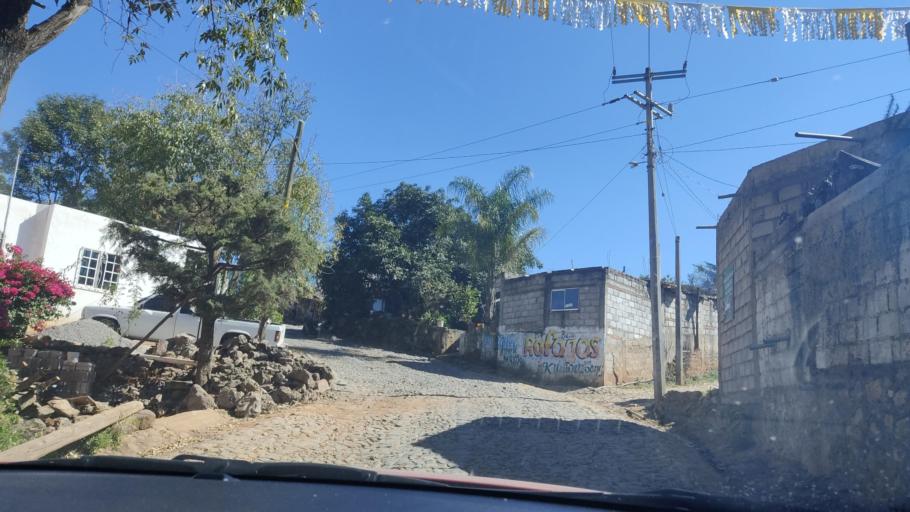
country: MX
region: Nayarit
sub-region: Jala
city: Rosa Blanca
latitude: 21.1018
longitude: -104.3422
